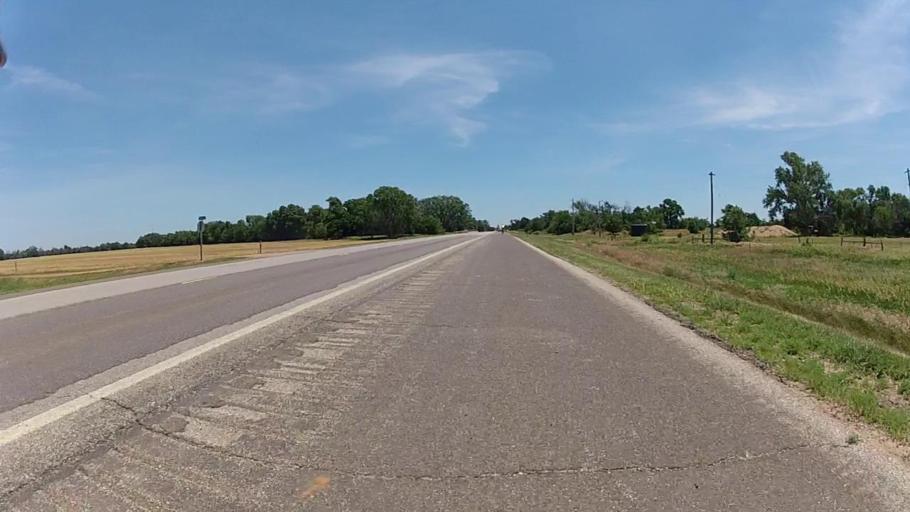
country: US
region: Kansas
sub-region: Barber County
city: Medicine Lodge
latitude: 37.2536
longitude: -98.4135
